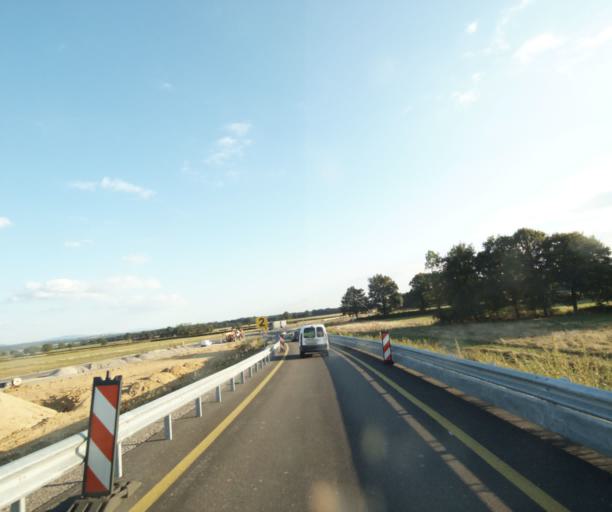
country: FR
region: Bourgogne
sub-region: Departement de Saone-et-Loire
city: Palinges
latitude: 46.5147
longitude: 4.1619
